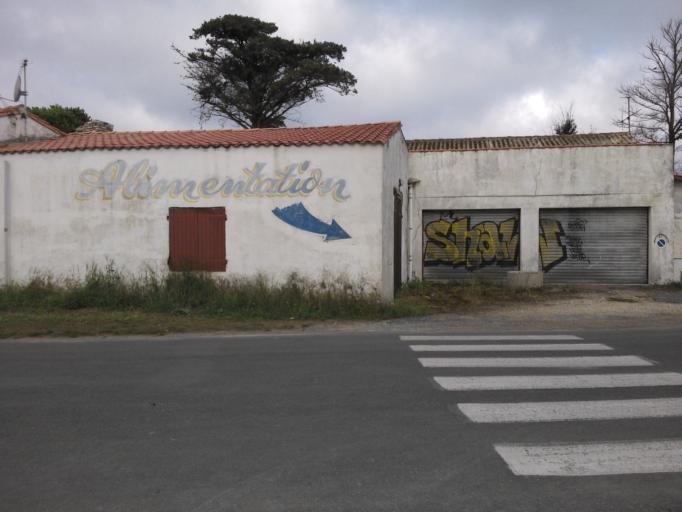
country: FR
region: Poitou-Charentes
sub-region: Departement de la Charente-Maritime
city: Saint-Denis-d'Oleron
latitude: 46.0161
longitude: -1.3927
